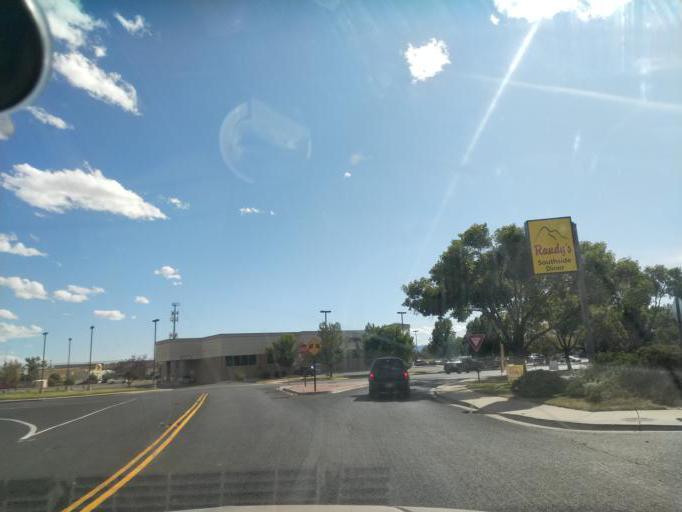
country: US
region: Colorado
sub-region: Mesa County
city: Clifton
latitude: 39.0888
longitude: -108.4594
